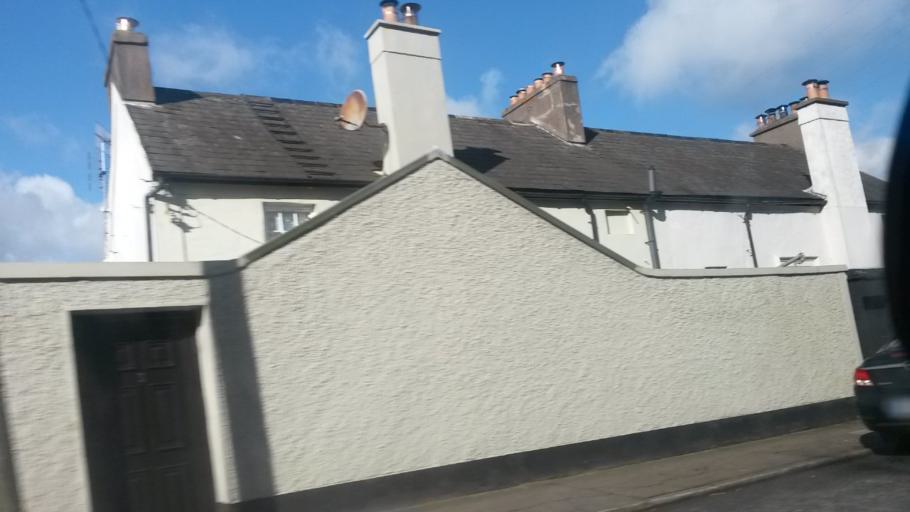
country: IE
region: Munster
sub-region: County Cork
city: Cobh
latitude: 51.8518
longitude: -8.3262
